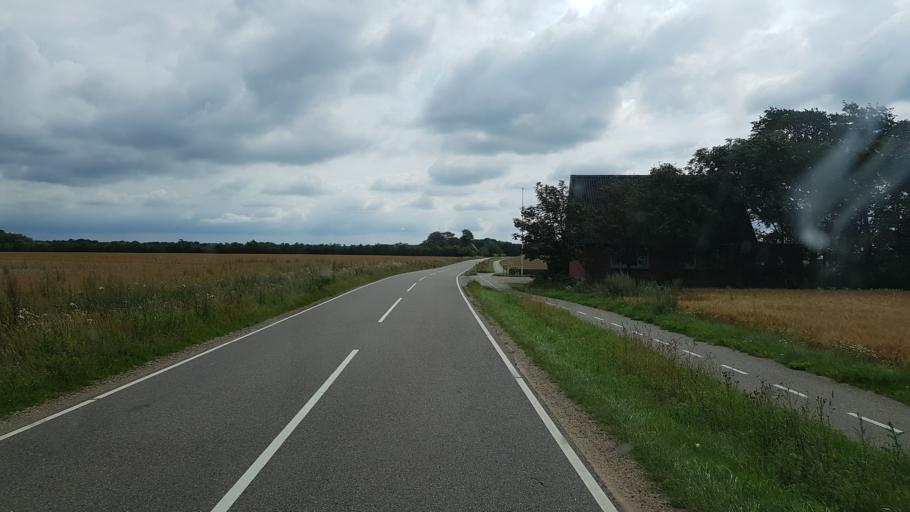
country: DK
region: South Denmark
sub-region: Varde Kommune
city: Varde
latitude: 55.7500
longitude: 8.4655
